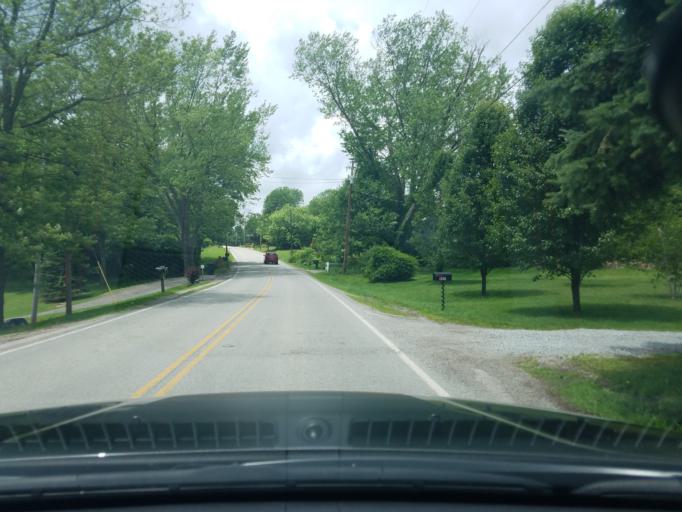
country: US
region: Pennsylvania
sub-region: Westmoreland County
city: Youngwood
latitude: 40.2199
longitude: -79.5615
